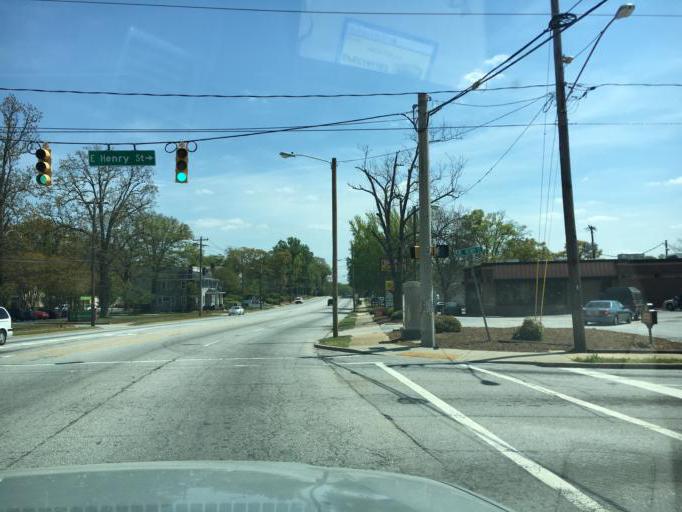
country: US
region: South Carolina
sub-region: Spartanburg County
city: Spartanburg
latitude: 34.9497
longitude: -81.9176
